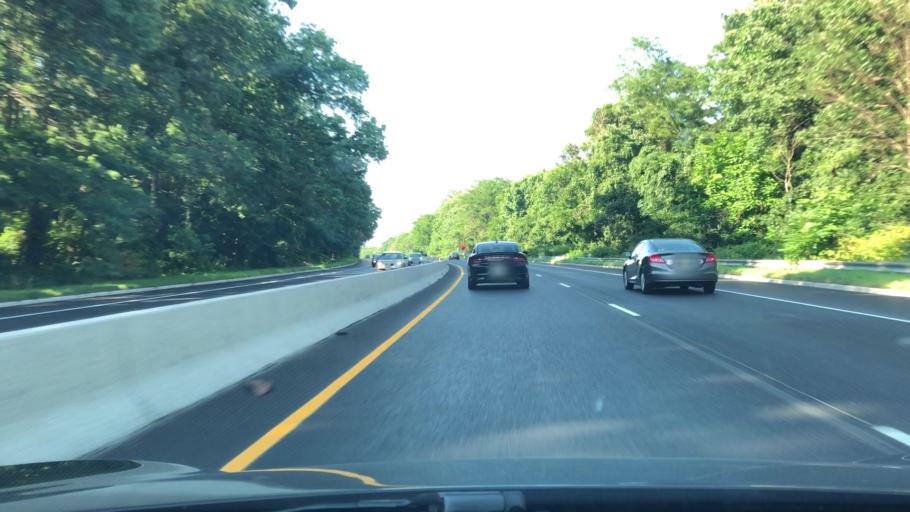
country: US
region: New Jersey
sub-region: Mercer County
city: Mercerville
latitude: 40.2540
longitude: -74.7200
